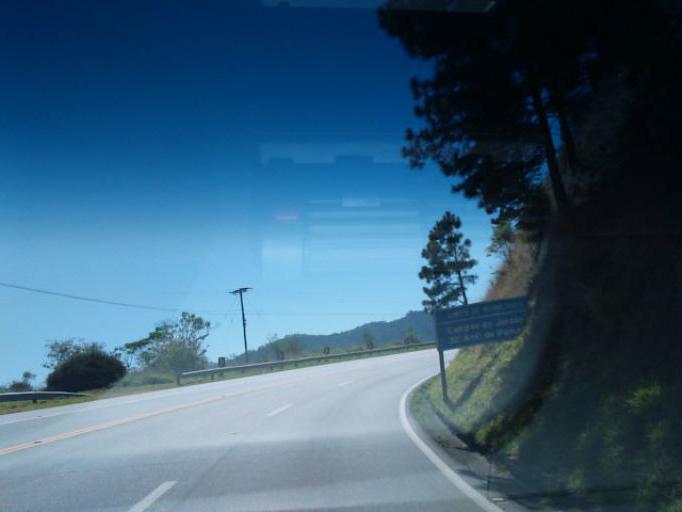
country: BR
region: Sao Paulo
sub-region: Campos Do Jordao
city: Campos do Jordao
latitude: -22.7929
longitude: -45.6288
